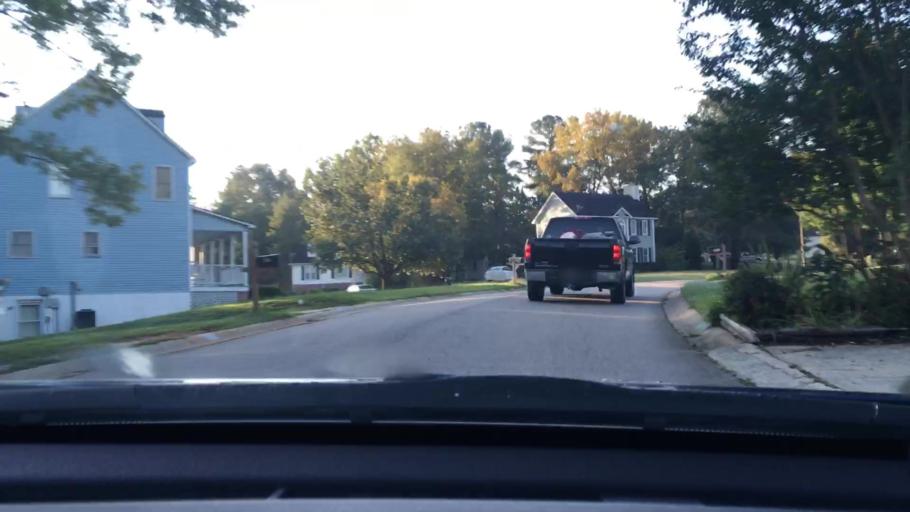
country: US
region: South Carolina
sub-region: Lexington County
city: Irmo
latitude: 34.1020
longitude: -81.1547
